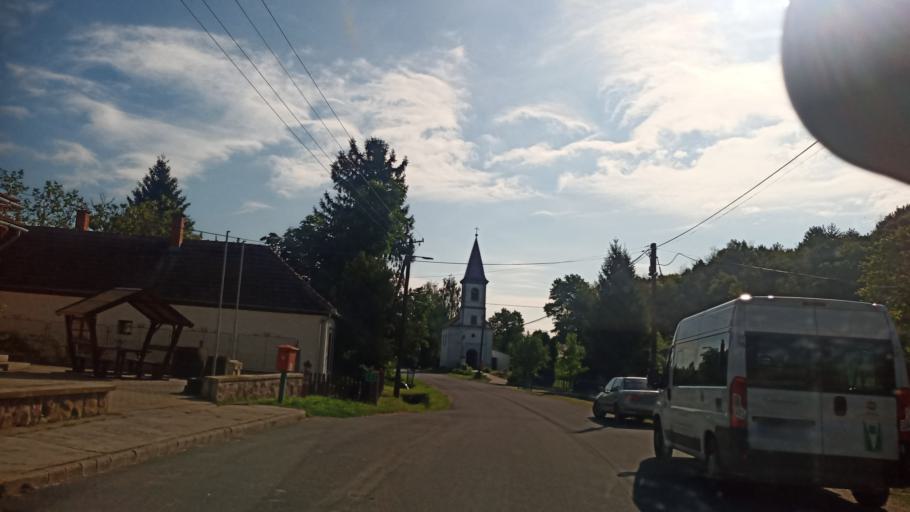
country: HU
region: Zala
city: Pacsa
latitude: 46.7042
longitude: 17.0644
